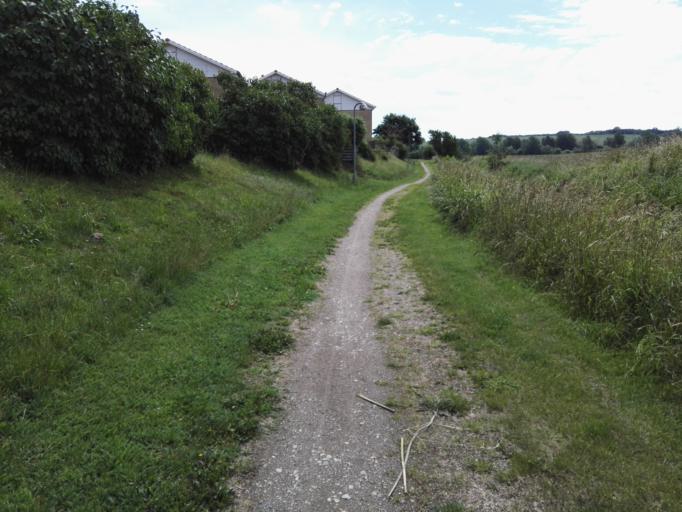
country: DK
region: Capital Region
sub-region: Frederikssund Kommune
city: Slangerup
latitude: 55.8395
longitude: 12.1826
